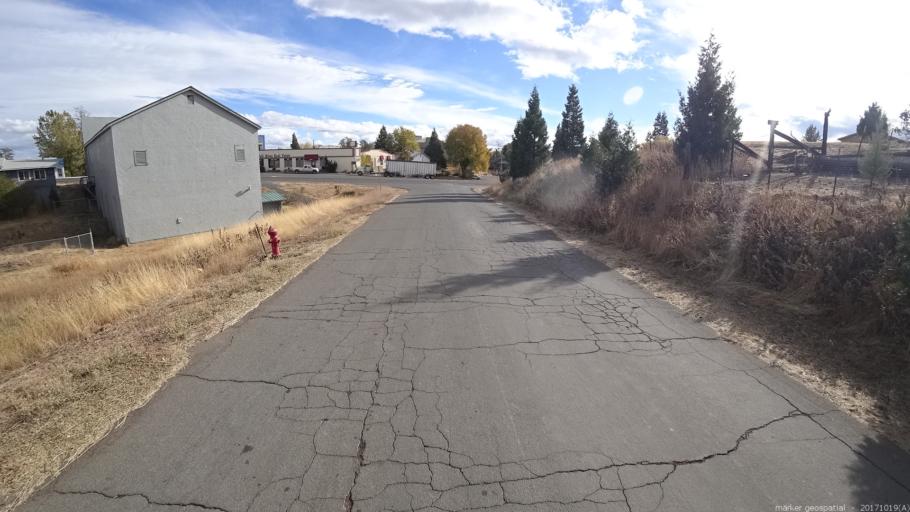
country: US
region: California
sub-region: Shasta County
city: Burney
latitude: 41.0045
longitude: -121.4395
